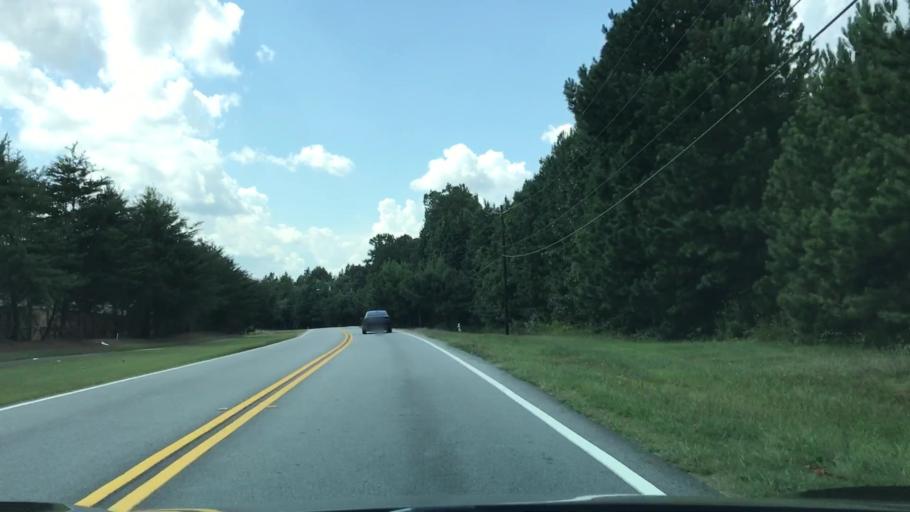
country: US
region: Georgia
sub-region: Gwinnett County
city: Snellville
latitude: 33.9066
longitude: -84.0674
